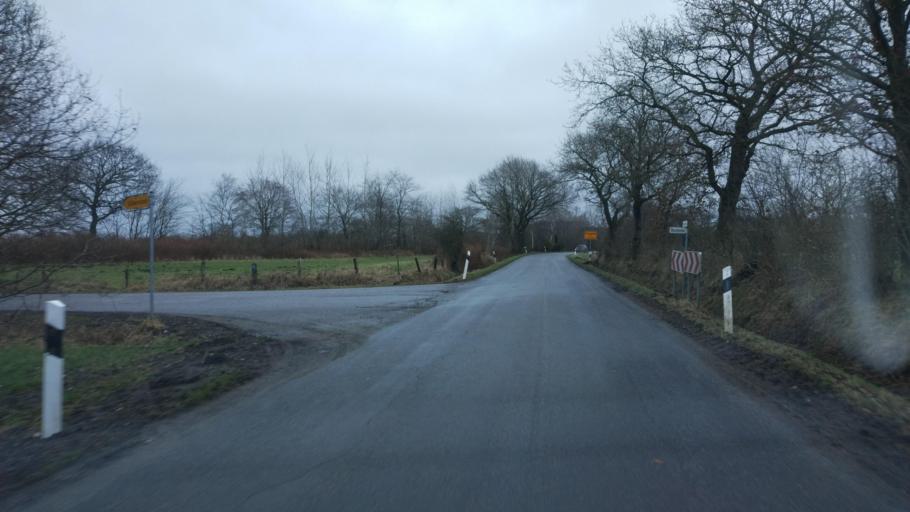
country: DE
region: Schleswig-Holstein
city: Ellingstedt
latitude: 54.4840
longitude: 9.4042
